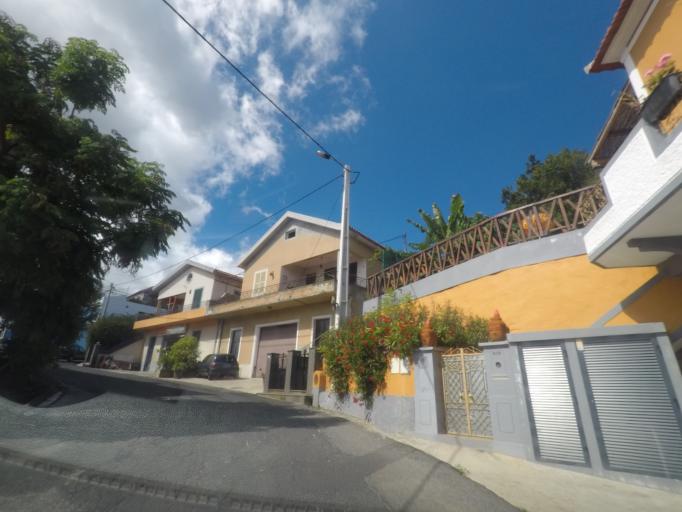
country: PT
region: Madeira
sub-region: Ribeira Brava
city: Campanario
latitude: 32.6682
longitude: -17.0496
